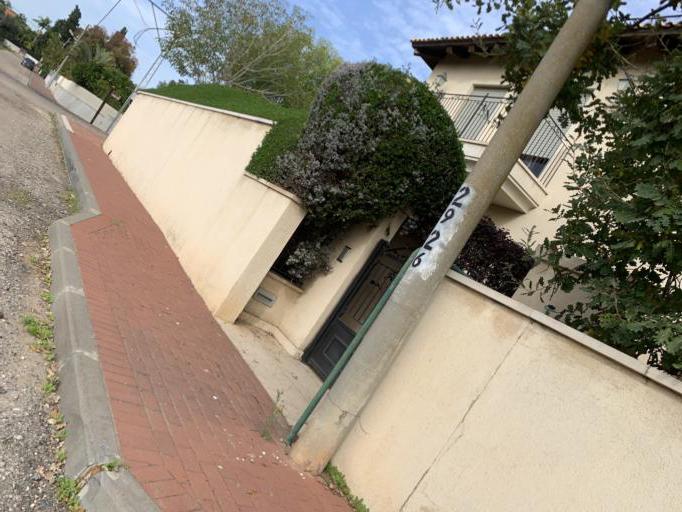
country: IL
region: Central District
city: Hod HaSharon
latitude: 32.1491
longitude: 34.9024
